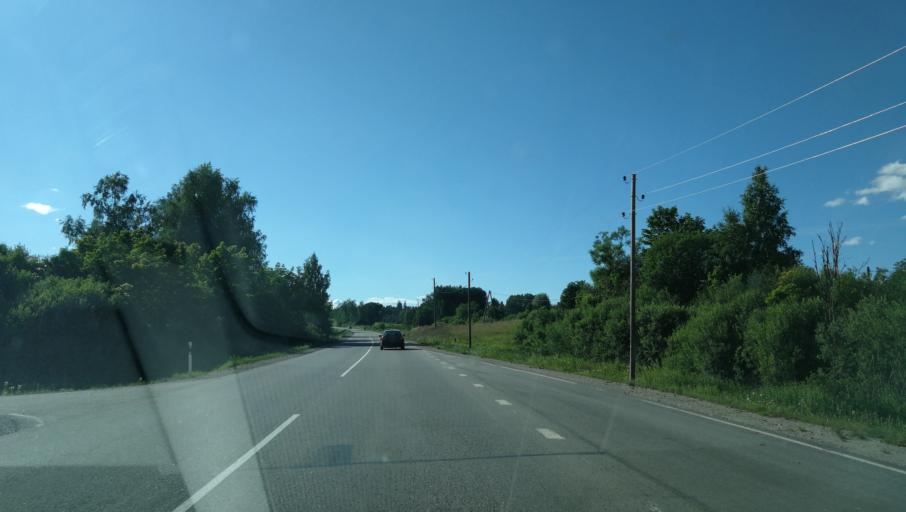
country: LV
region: Vecpiebalga
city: Vecpiebalga
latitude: 57.1068
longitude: 25.7117
